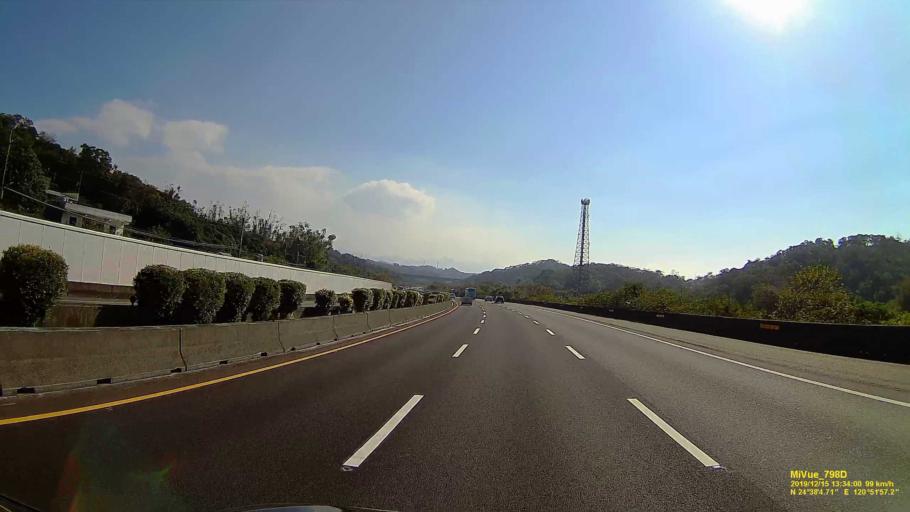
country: TW
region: Taiwan
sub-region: Miaoli
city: Miaoli
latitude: 24.6340
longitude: 120.8661
